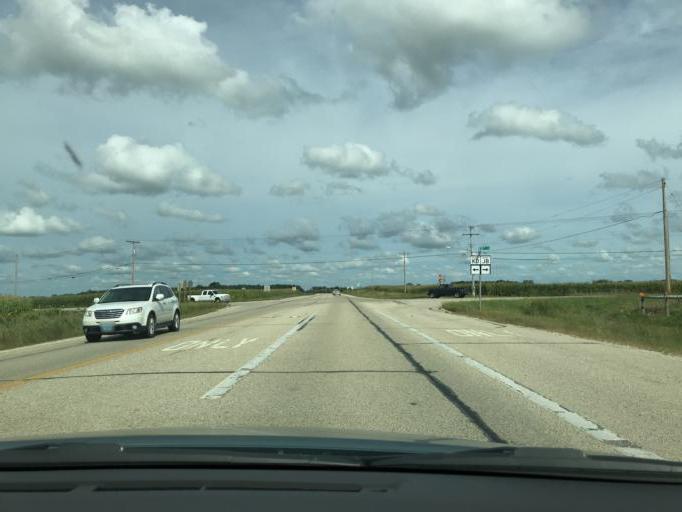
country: US
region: Wisconsin
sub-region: Racine County
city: Bohners Lake
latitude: 42.6103
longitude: -88.2291
